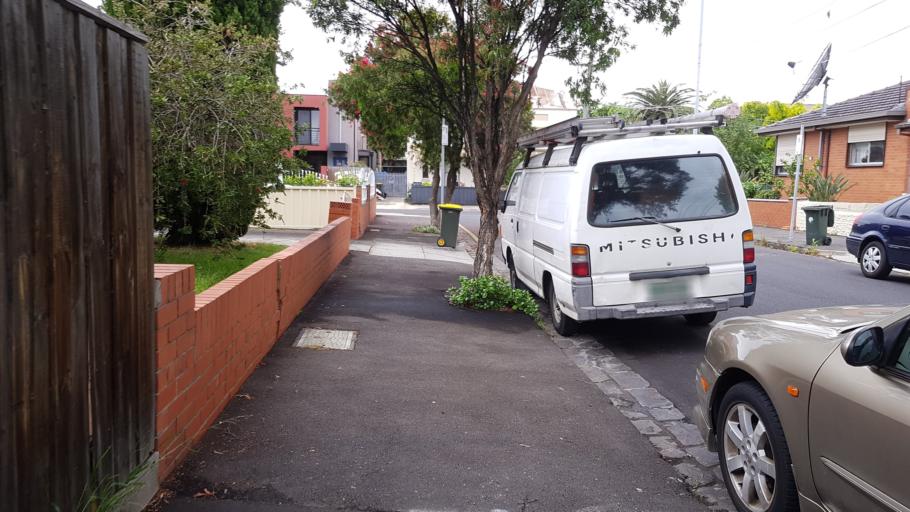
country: AU
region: Victoria
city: Brunswick East
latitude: -37.7718
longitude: 144.9745
